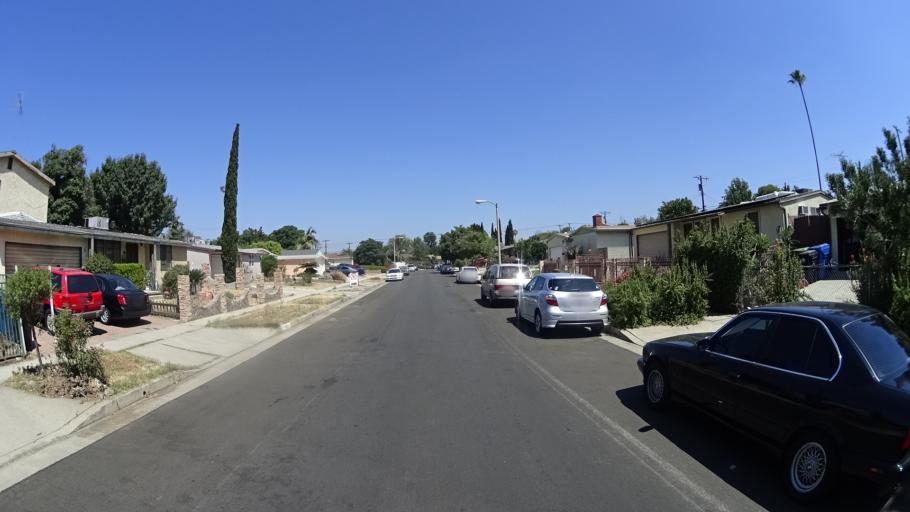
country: US
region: California
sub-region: Los Angeles County
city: Van Nuys
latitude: 34.2284
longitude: -118.4377
